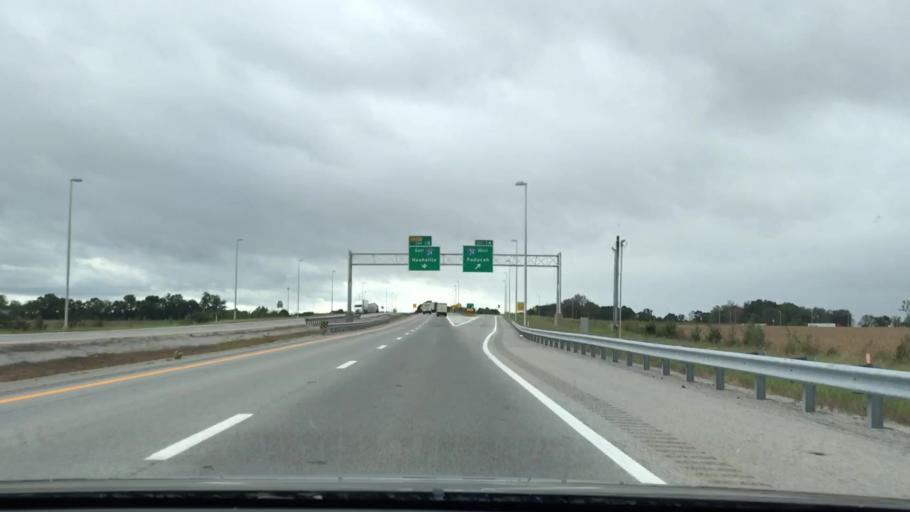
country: US
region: Kentucky
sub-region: Christian County
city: Fort Campbell North
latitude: 36.7498
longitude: -87.5095
